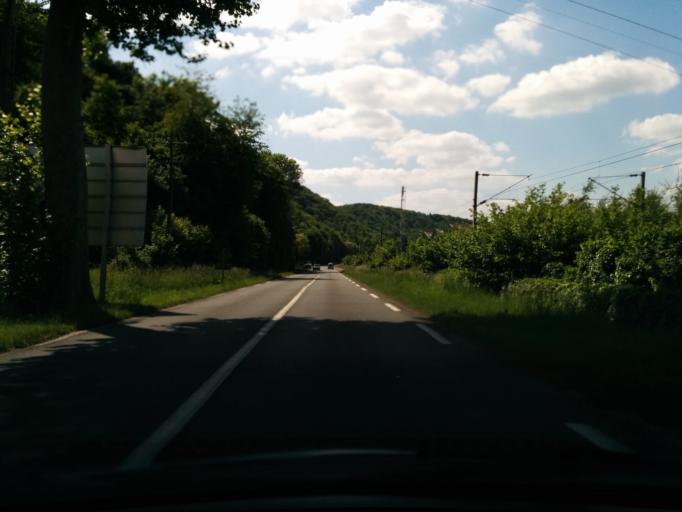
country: FR
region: Ile-de-France
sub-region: Departement des Yvelines
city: Bennecourt
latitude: 49.0330
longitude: 1.5595
